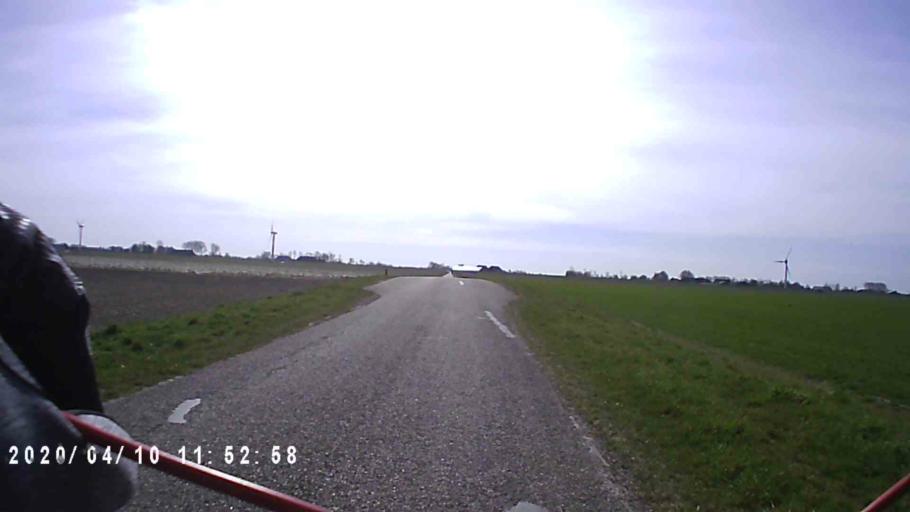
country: NL
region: Groningen
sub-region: Gemeente De Marne
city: Ulrum
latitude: 53.3924
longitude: 6.3321
